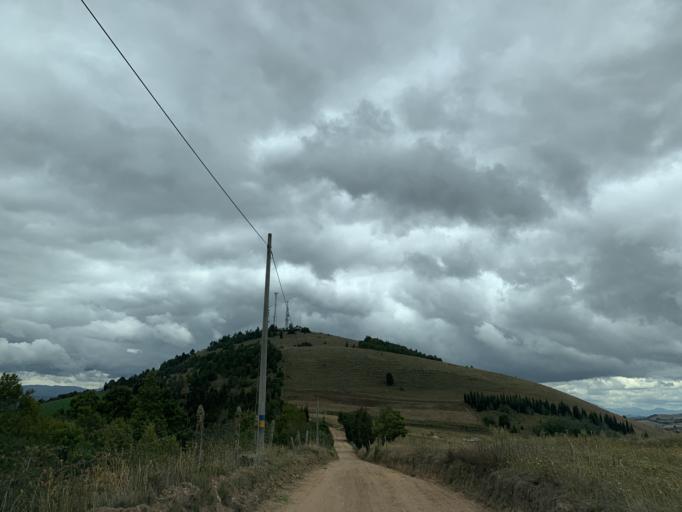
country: CO
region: Boyaca
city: Tunja
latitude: 5.5366
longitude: -73.3206
